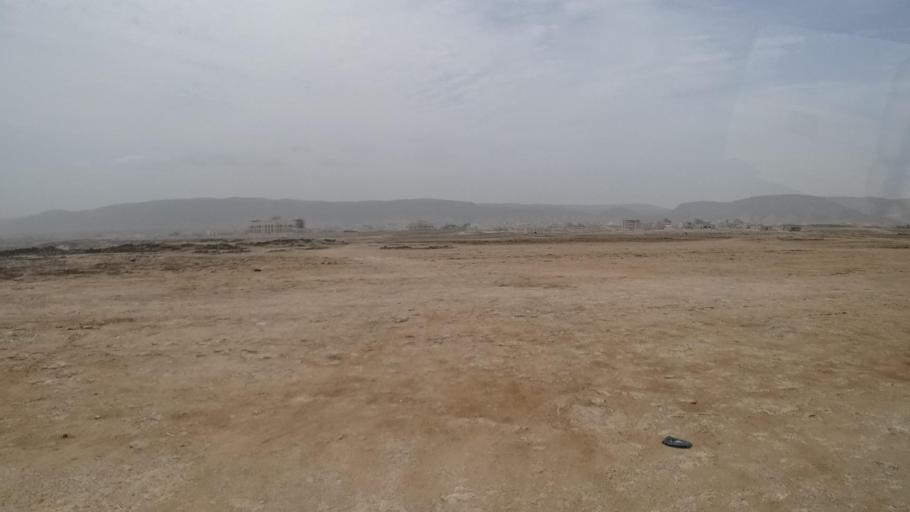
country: OM
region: Zufar
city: Salalah
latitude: 17.0324
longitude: 54.4101
